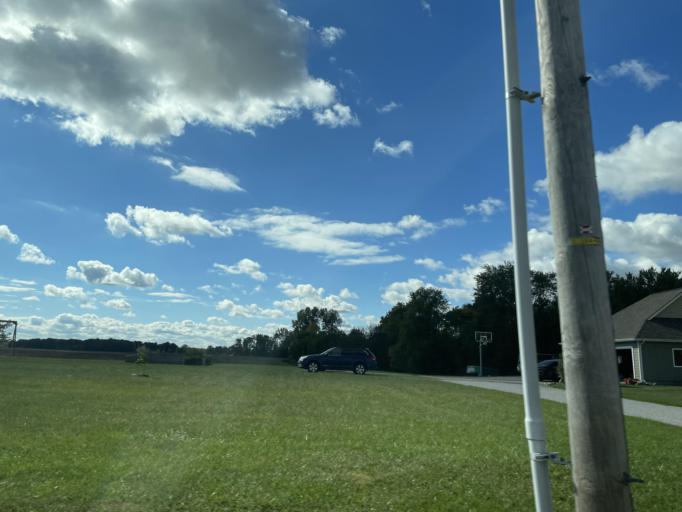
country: US
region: Indiana
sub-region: Whitley County
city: Churubusco
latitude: 41.1187
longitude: -85.2624
